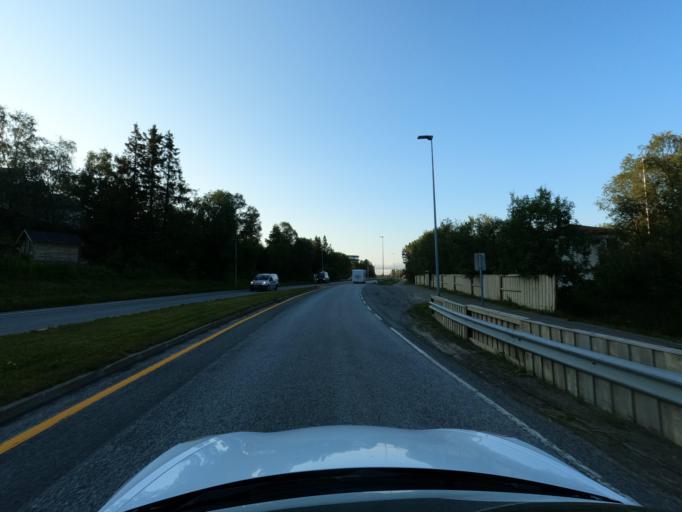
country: NO
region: Troms
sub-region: Harstad
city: Harstad
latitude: 68.7548
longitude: 16.5660
